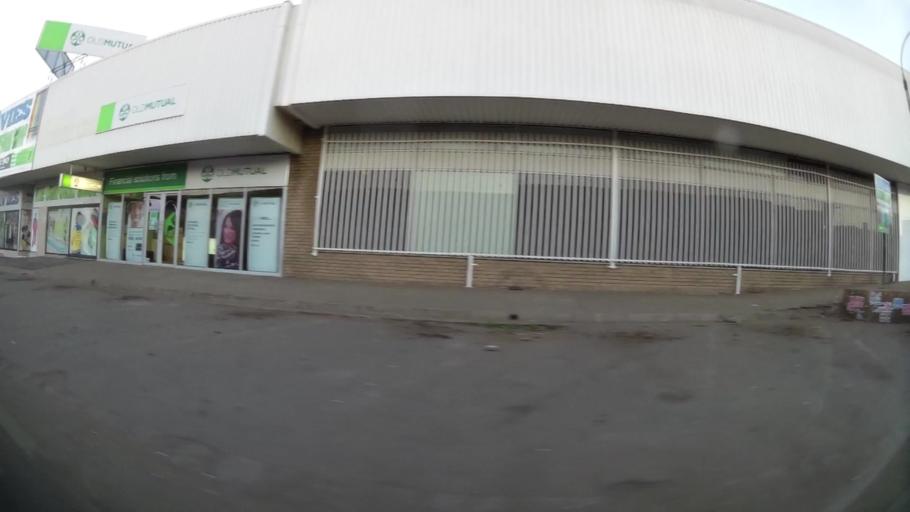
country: ZA
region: North-West
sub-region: Bojanala Platinum District Municipality
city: Rustenburg
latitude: -25.6653
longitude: 27.2397
